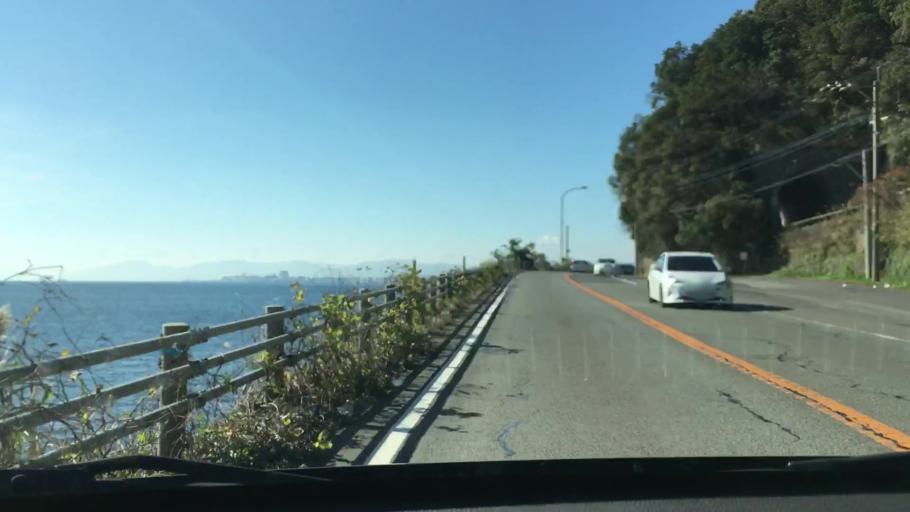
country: JP
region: Kagoshima
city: Kagoshima-shi
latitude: 31.6267
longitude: 130.5956
